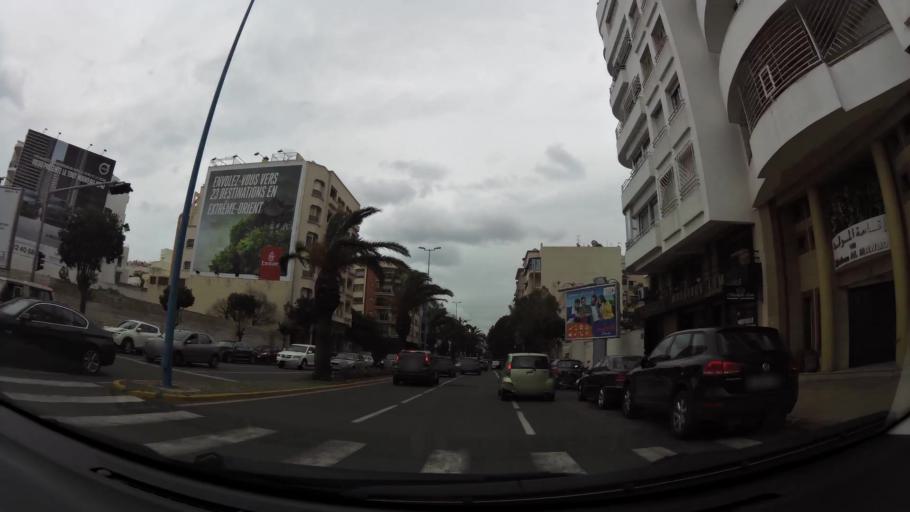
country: MA
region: Grand Casablanca
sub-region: Casablanca
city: Casablanca
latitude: 33.5906
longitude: -7.6452
